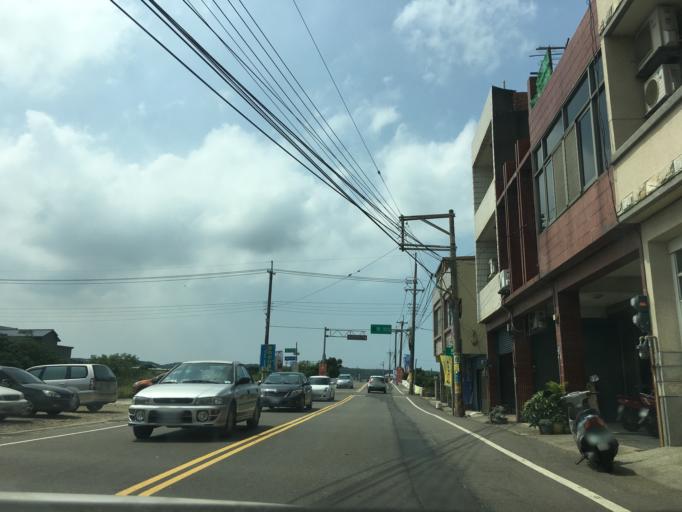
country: TW
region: Taiwan
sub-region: Hsinchu
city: Zhubei
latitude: 24.9019
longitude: 120.9839
